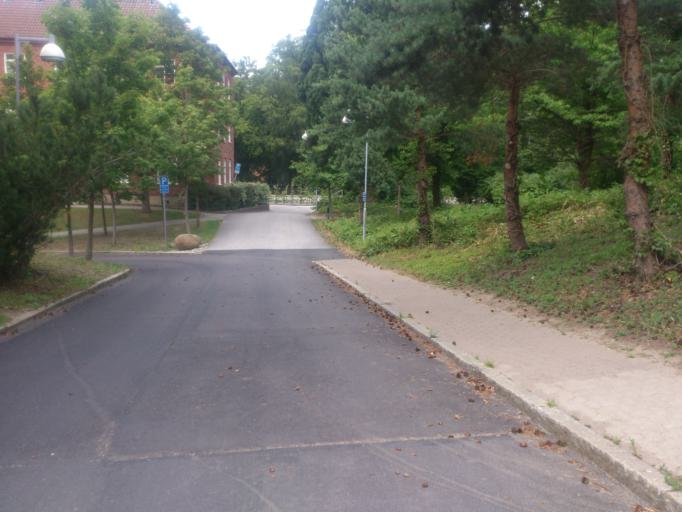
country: SE
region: Skane
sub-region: Lunds Kommun
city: Lund
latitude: 55.7112
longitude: 13.1950
